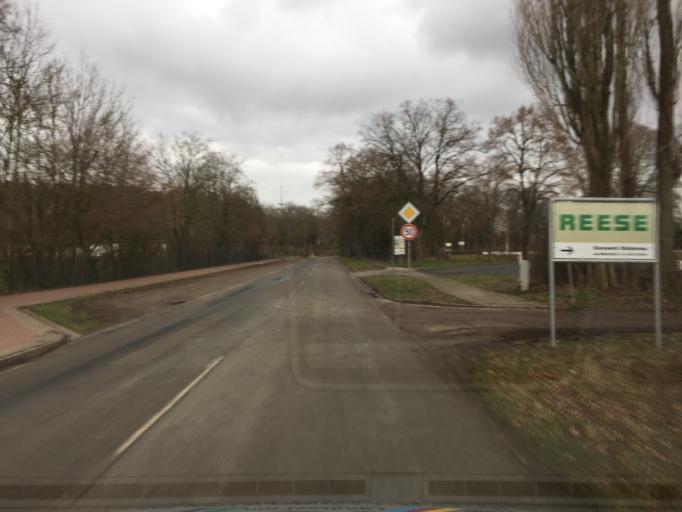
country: DE
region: Lower Saxony
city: Stolzenau
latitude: 52.5058
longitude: 9.0741
